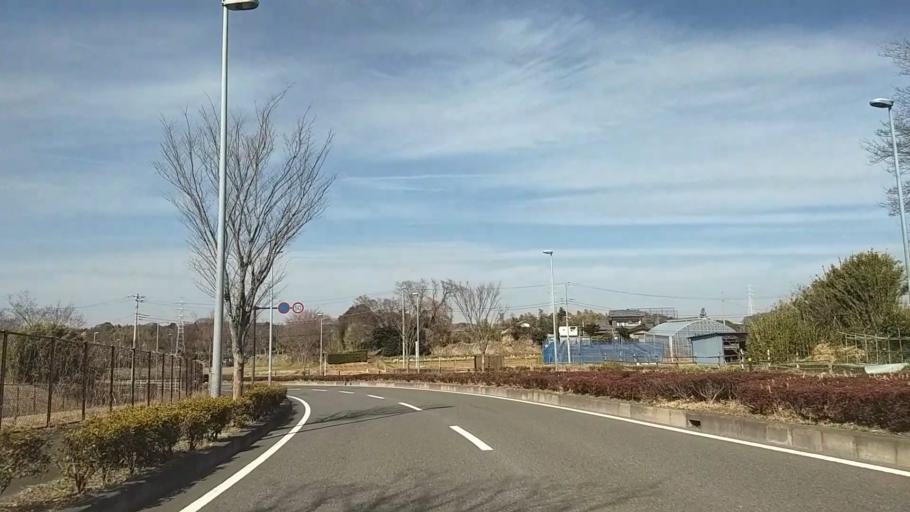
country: JP
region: Kanagawa
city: Fujisawa
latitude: 35.3800
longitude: 139.4324
